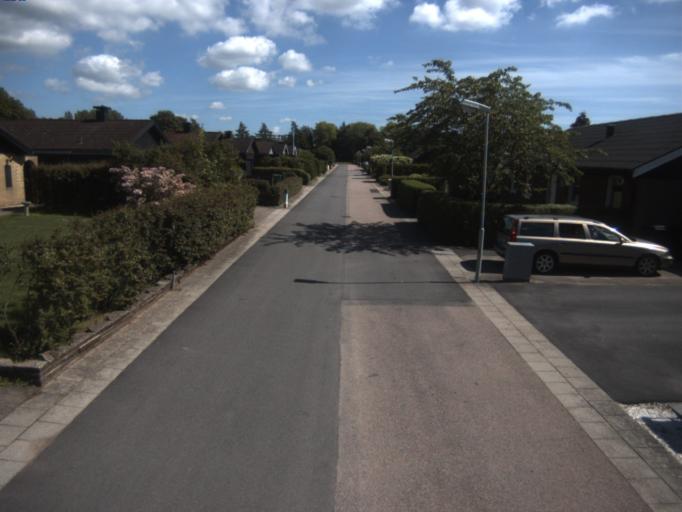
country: SE
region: Skane
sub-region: Helsingborg
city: Odakra
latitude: 56.0718
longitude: 12.7320
